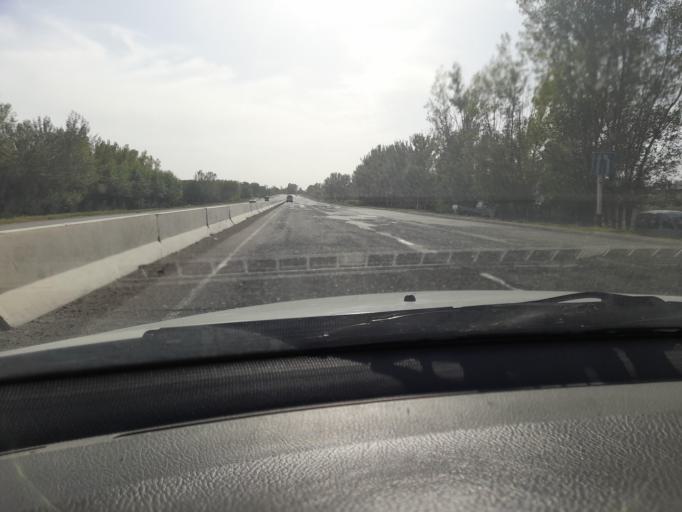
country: UZ
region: Samarqand
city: Kattaqo'rg'on
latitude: 39.9170
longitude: 66.3262
